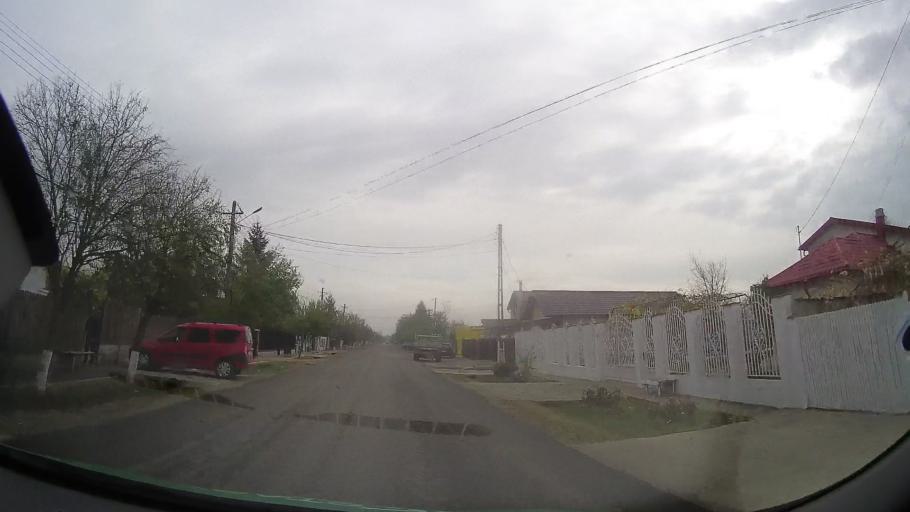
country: RO
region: Prahova
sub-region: Comuna Dumbrava
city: Dumbrava
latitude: 44.8705
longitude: 26.1939
